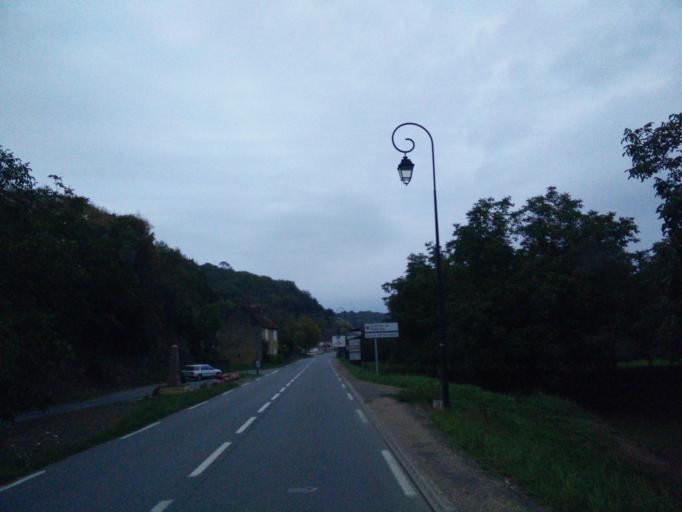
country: FR
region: Aquitaine
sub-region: Departement de la Dordogne
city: Carsac-Aillac
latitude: 44.8225
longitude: 1.2891
